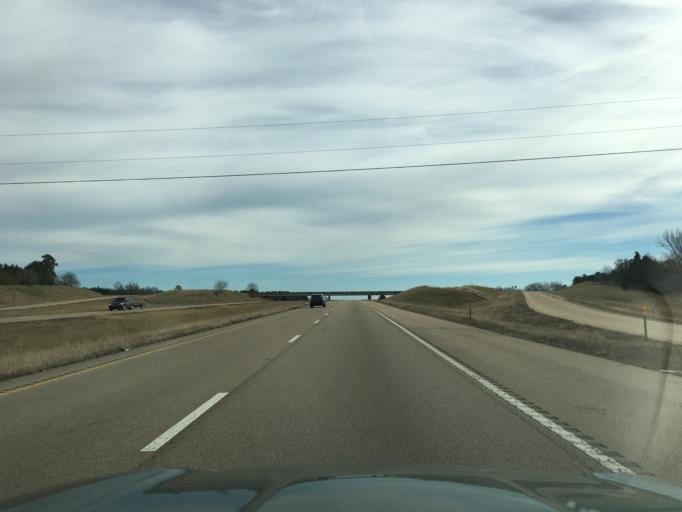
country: US
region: Mississippi
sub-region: Marshall County
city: Holly Springs
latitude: 34.6824
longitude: -89.3685
